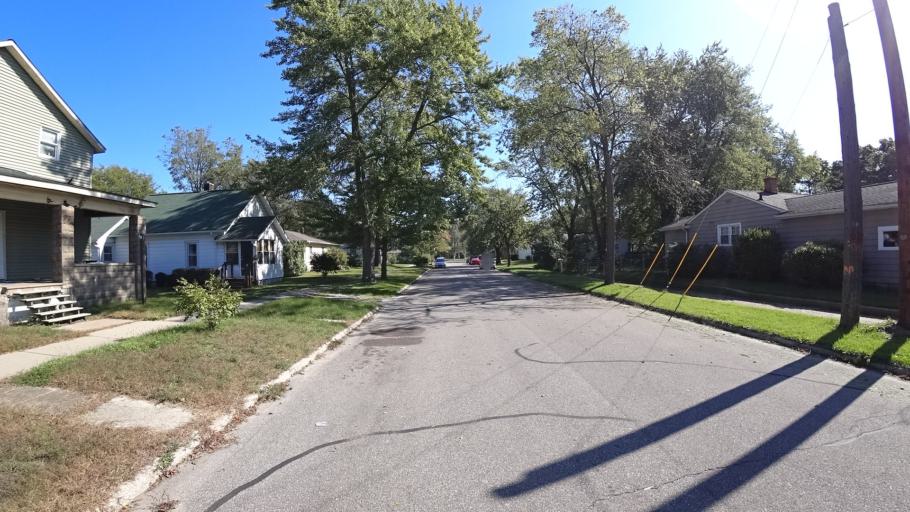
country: US
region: Indiana
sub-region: LaPorte County
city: Michigan City
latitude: 41.7083
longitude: -86.8860
